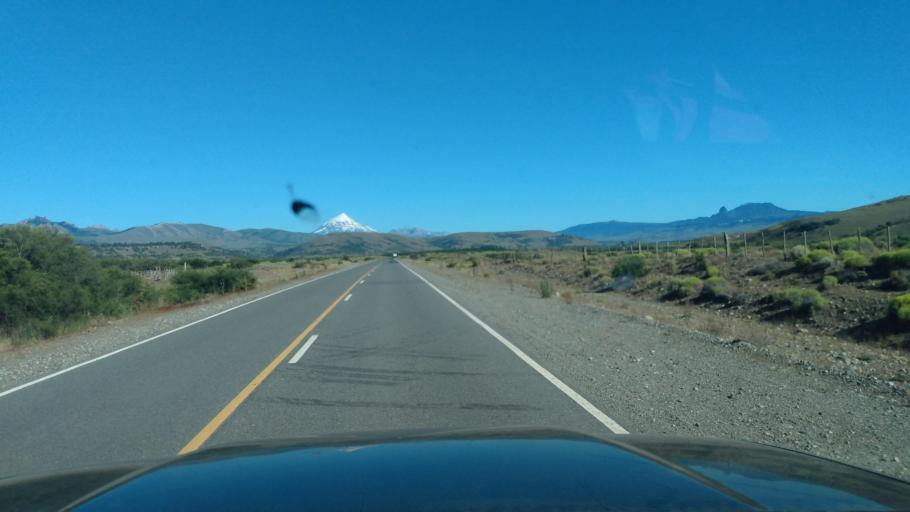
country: AR
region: Neuquen
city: Junin de los Andes
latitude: -39.8837
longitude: -71.1601
